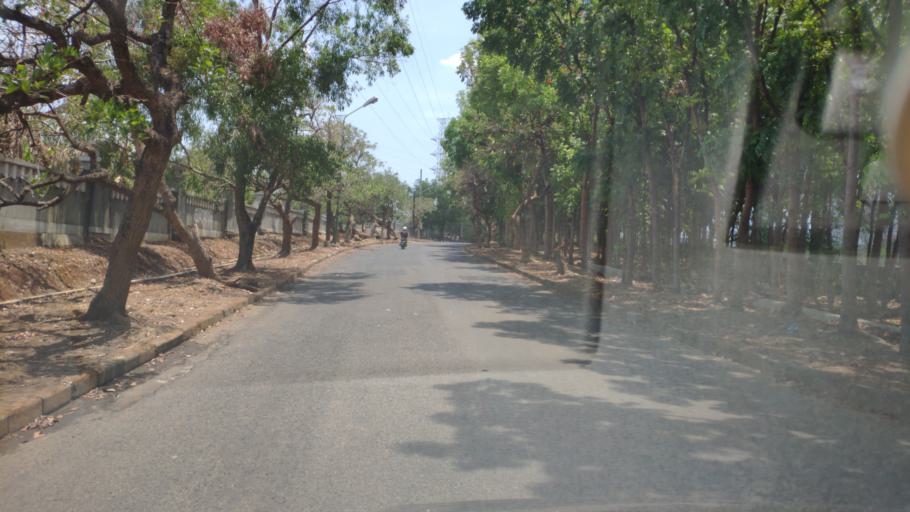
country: ID
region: Central Java
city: Semarang
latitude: -7.0478
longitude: 110.4348
